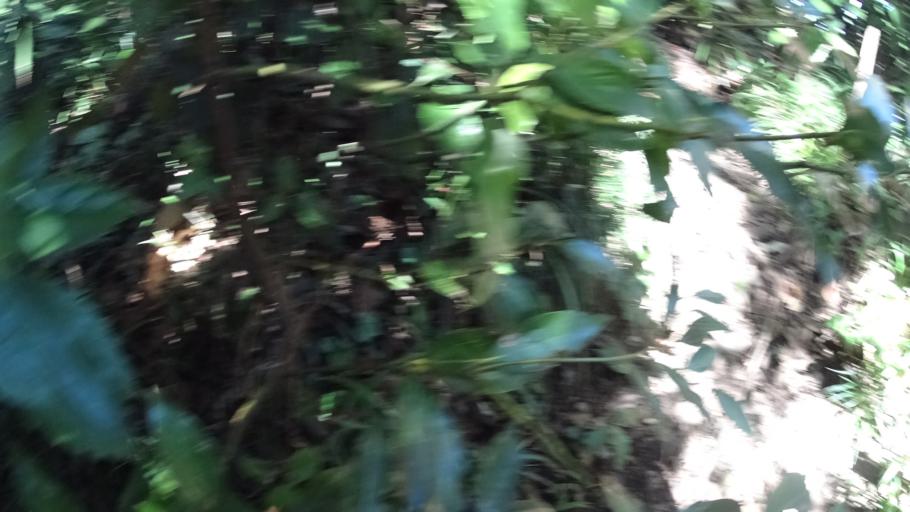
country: JP
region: Kanagawa
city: Hayama
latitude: 35.2789
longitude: 139.6088
